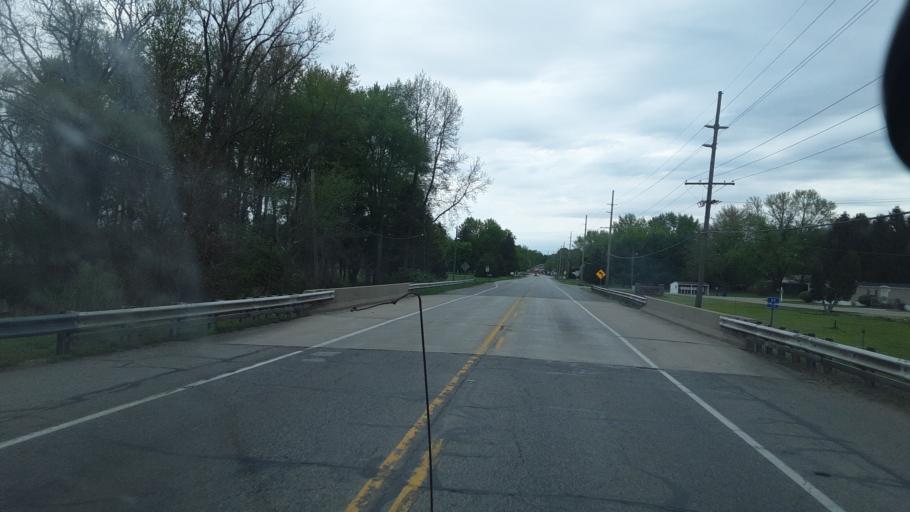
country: US
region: Indiana
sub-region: Elkhart County
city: Goshen
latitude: 41.6397
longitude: -85.8252
